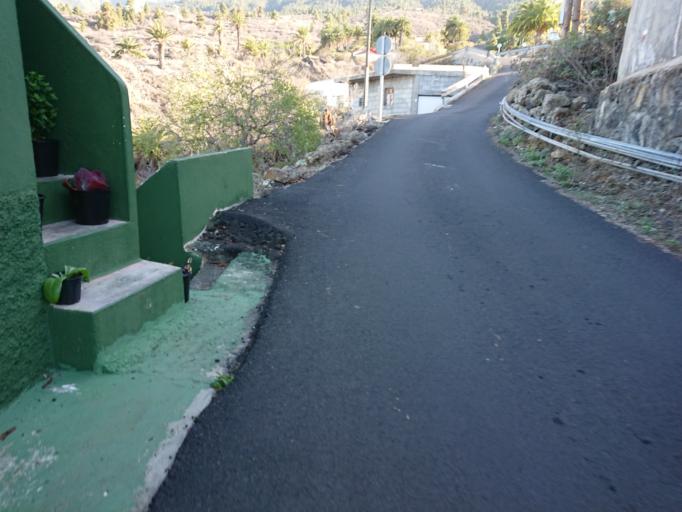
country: ES
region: Canary Islands
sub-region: Provincia de Santa Cruz de Tenerife
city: Tijarafe
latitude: 28.6799
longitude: -17.9453
